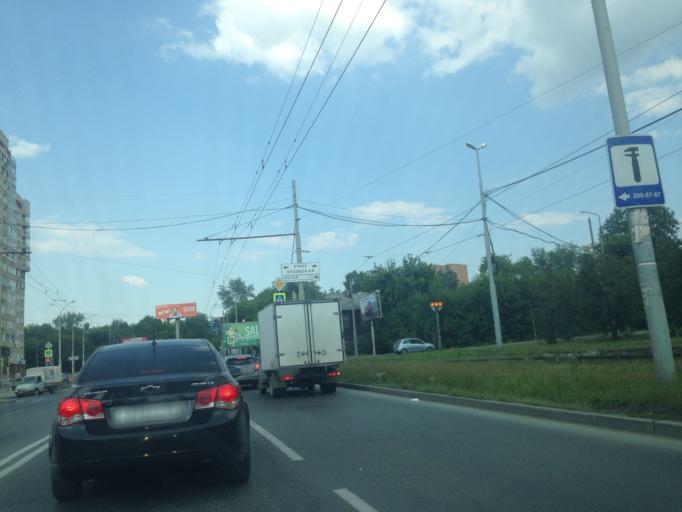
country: RU
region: Sverdlovsk
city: Yekaterinburg
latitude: 56.8609
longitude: 60.6239
